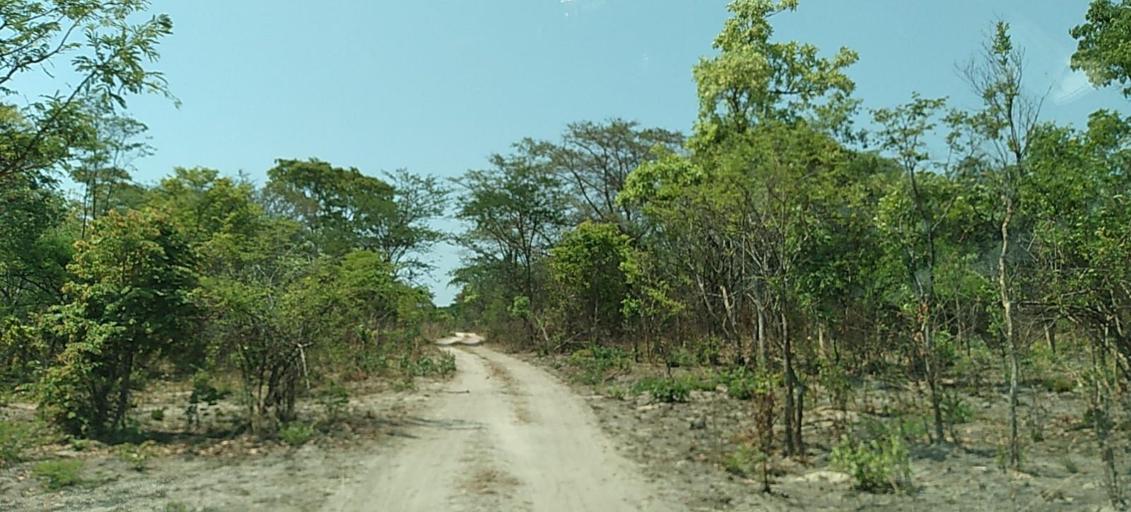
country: ZM
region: Copperbelt
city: Mpongwe
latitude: -13.8339
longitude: 28.0595
